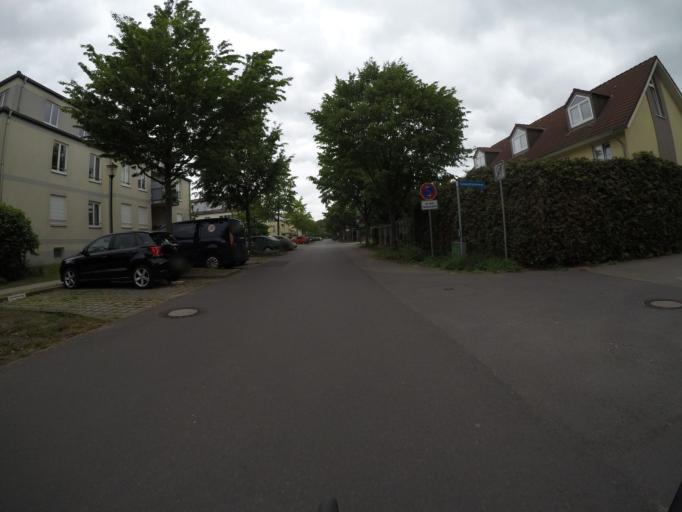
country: DE
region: Brandenburg
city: Glienicke
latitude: 52.6358
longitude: 13.3213
